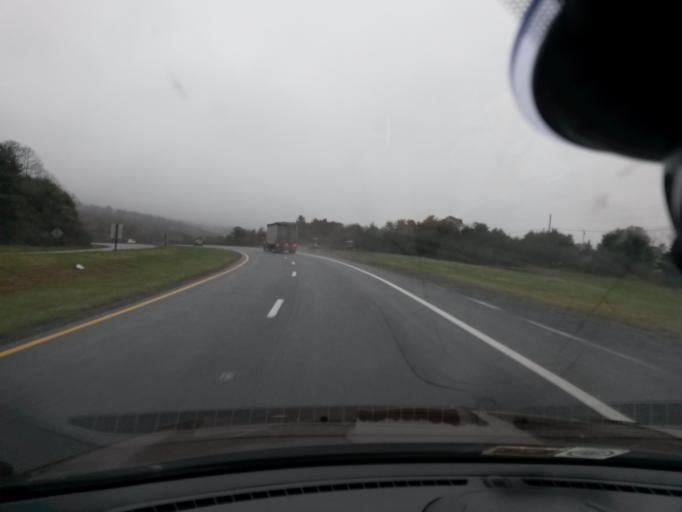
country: US
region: Virginia
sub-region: Botetourt County
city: Fincastle
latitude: 37.5574
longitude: -79.8467
